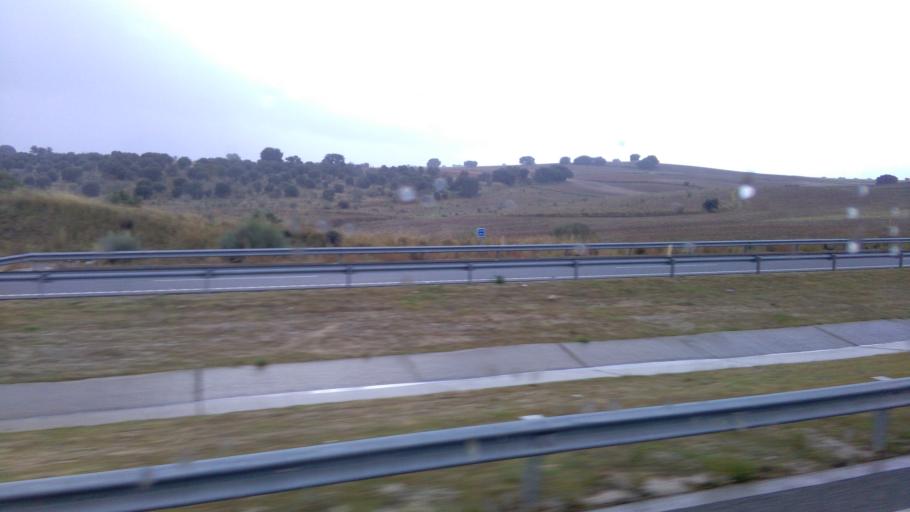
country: ES
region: Madrid
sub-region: Provincia de Madrid
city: El Alamo
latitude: 40.2619
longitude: -3.9658
